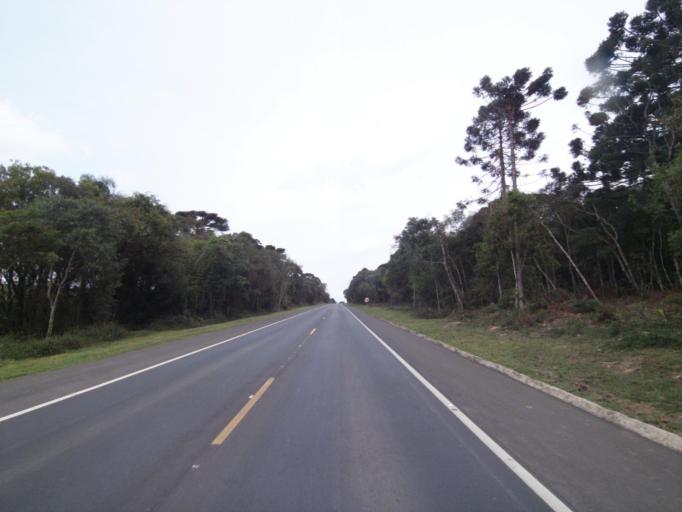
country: BR
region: Parana
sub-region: Irati
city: Irati
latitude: -25.4640
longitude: -50.5450
